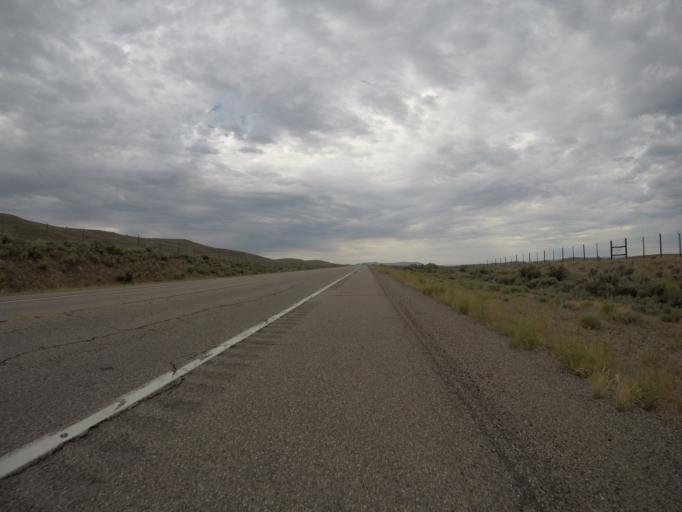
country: US
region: Utah
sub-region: Rich County
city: Randolph
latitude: 41.8342
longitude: -110.9794
